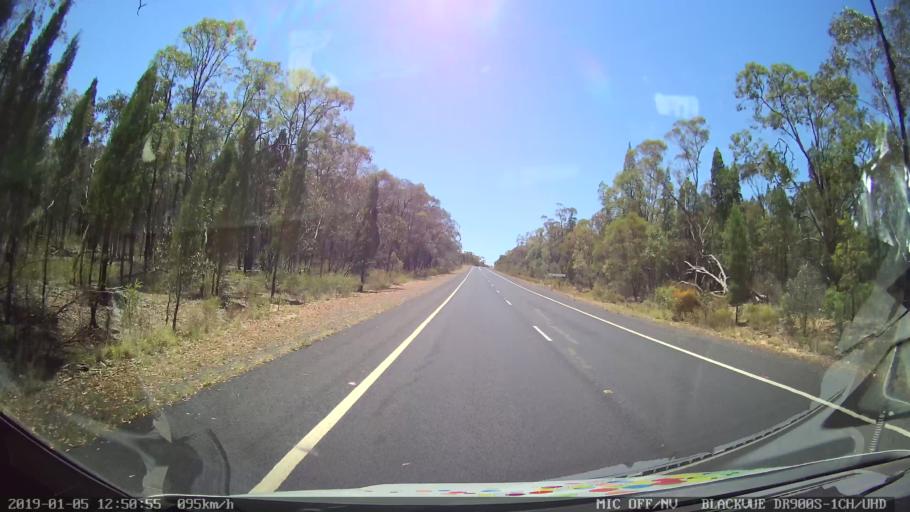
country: AU
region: New South Wales
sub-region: Warrumbungle Shire
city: Coonabarabran
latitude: -31.1205
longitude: 149.6312
